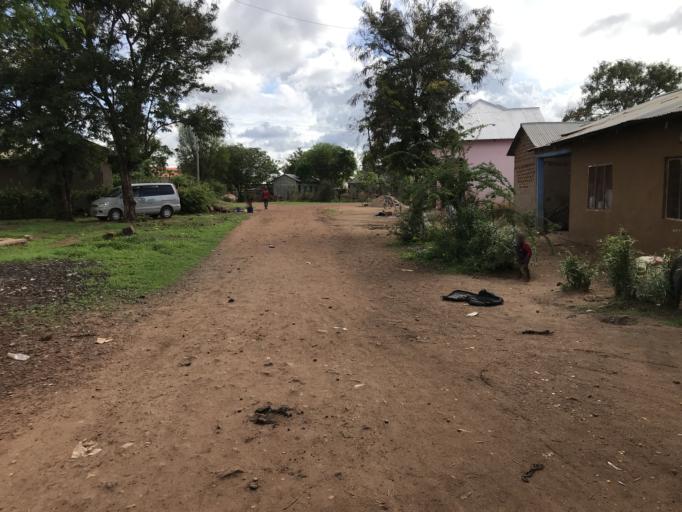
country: TZ
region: Tabora
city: Igunga
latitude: -4.2889
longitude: 33.8823
